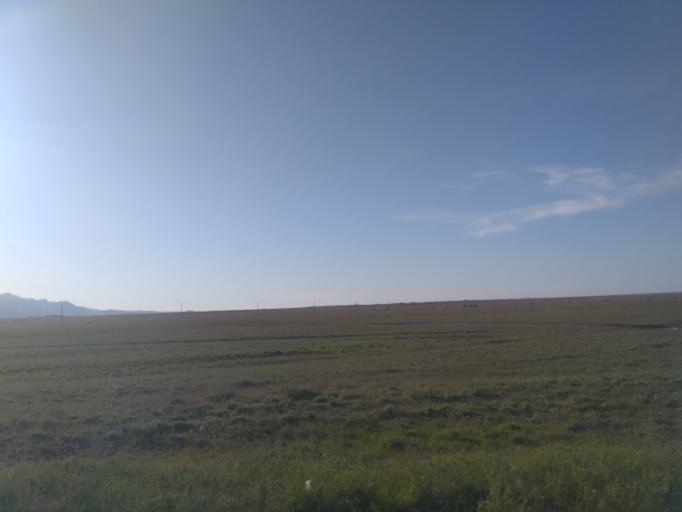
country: KZ
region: Ongtustik Qazaqstan
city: Ashchysay
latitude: 43.6954
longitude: 68.9984
